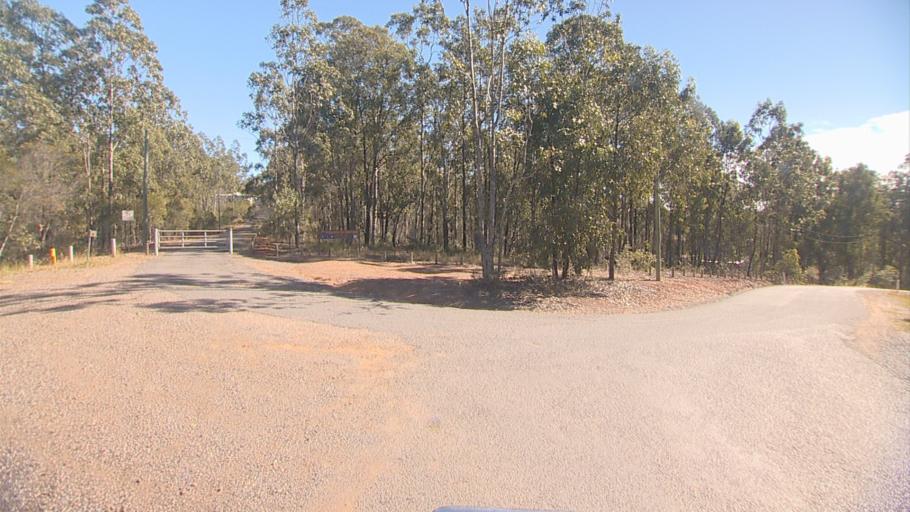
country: AU
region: Queensland
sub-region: Ipswich
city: Springfield Lakes
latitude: -27.7208
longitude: 152.9132
